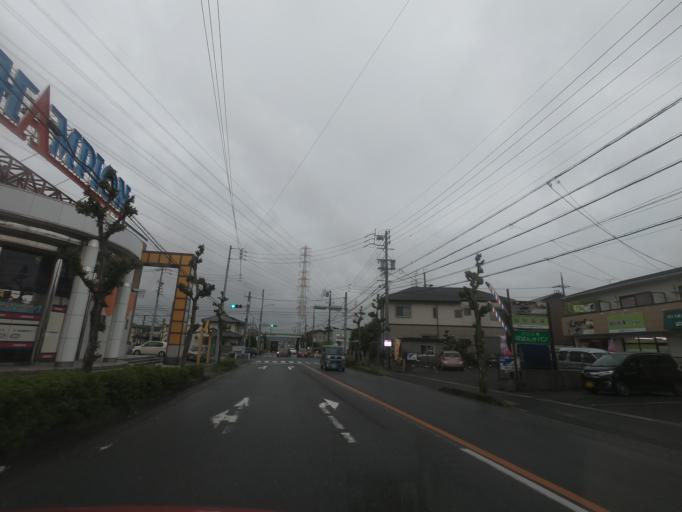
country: JP
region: Aichi
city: Kasugai
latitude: 35.2578
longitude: 136.9974
